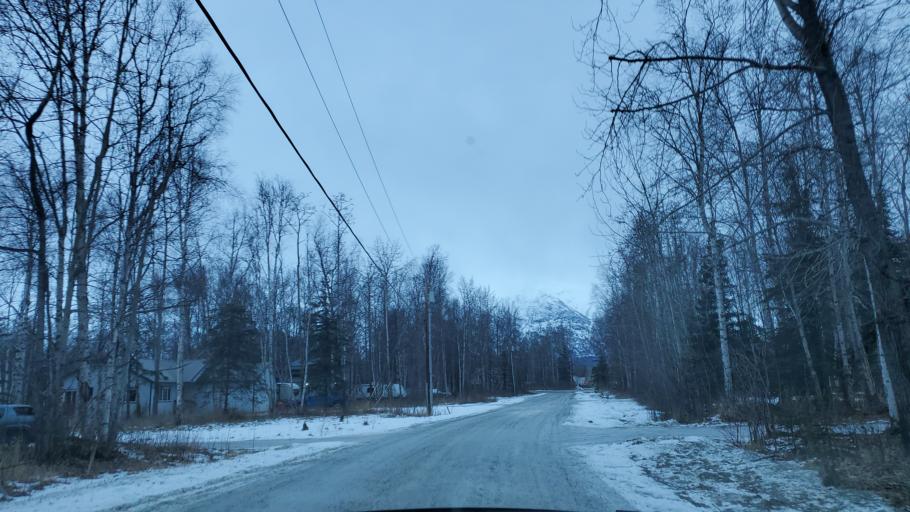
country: US
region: Alaska
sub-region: Matanuska-Susitna Borough
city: Lakes
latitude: 61.6657
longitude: -149.3020
